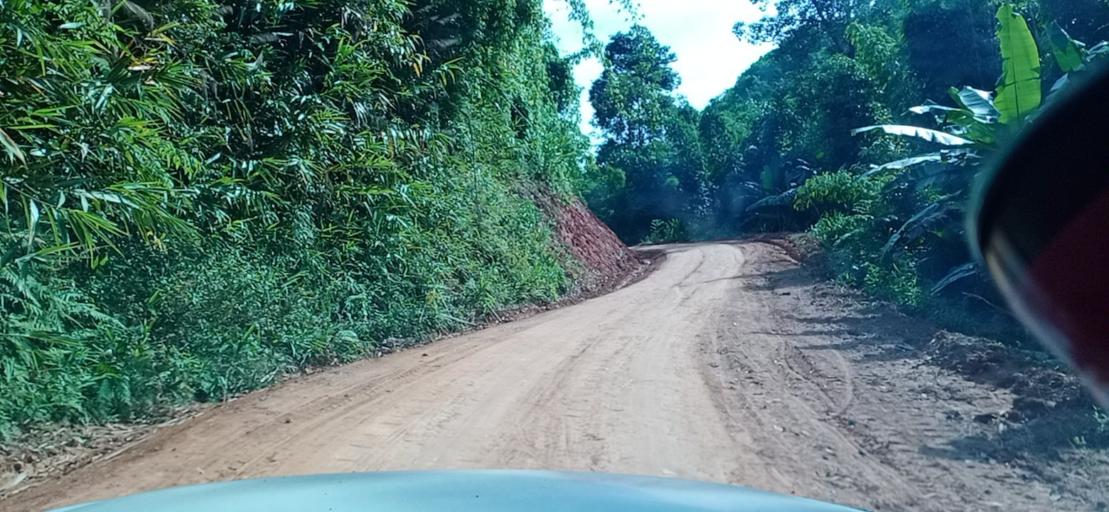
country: TH
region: Changwat Bueng Kan
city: Pak Khat
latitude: 18.6382
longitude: 103.2397
